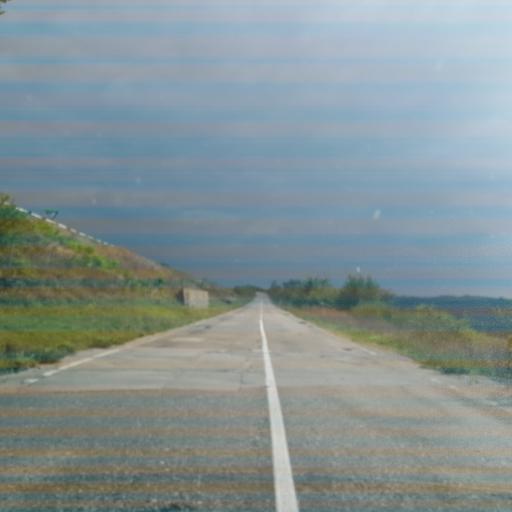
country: RS
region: Central Serbia
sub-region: Nisavski Okrug
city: Razanj
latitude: 43.6430
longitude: 21.5556
